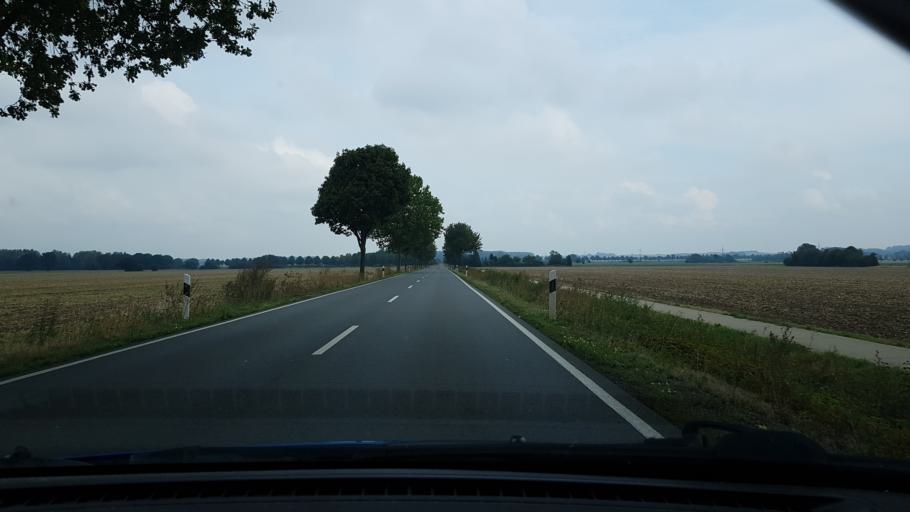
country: DE
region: Lower Saxony
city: Barsinghausen
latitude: 52.3229
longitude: 9.4674
